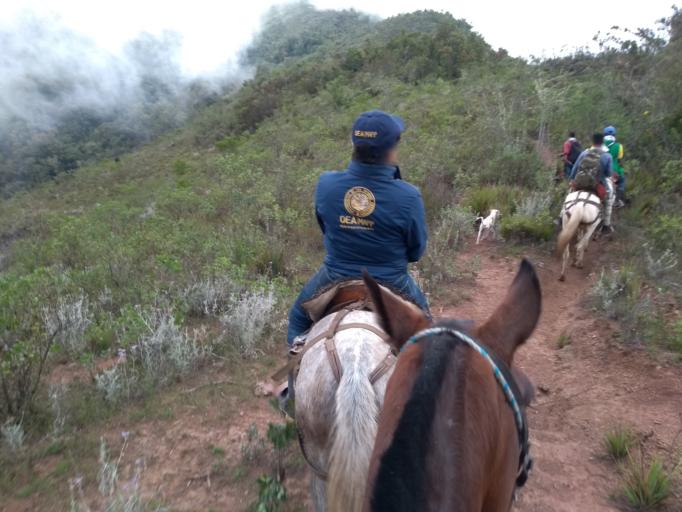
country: CO
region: Cesar
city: Manaure Balcon del Cesar
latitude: 10.2150
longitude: -73.0110
